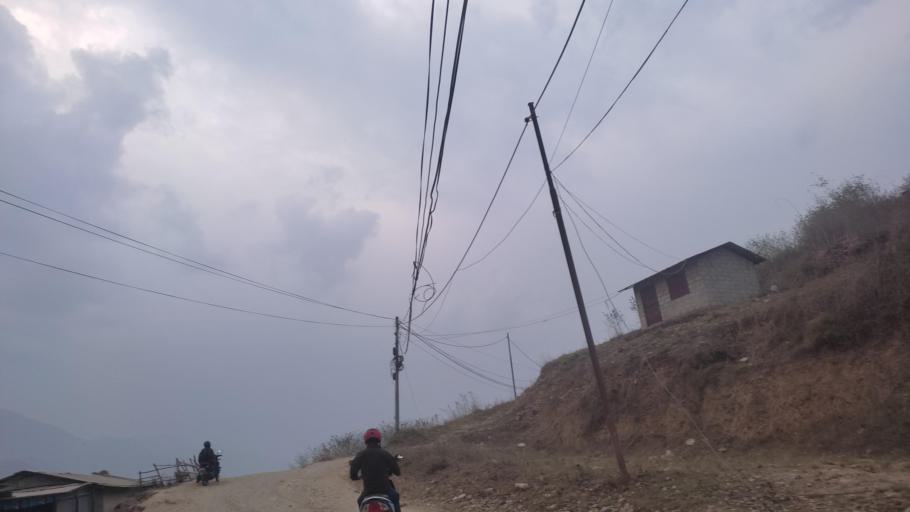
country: NP
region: Central Region
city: Kirtipur
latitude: 27.6633
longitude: 85.2882
